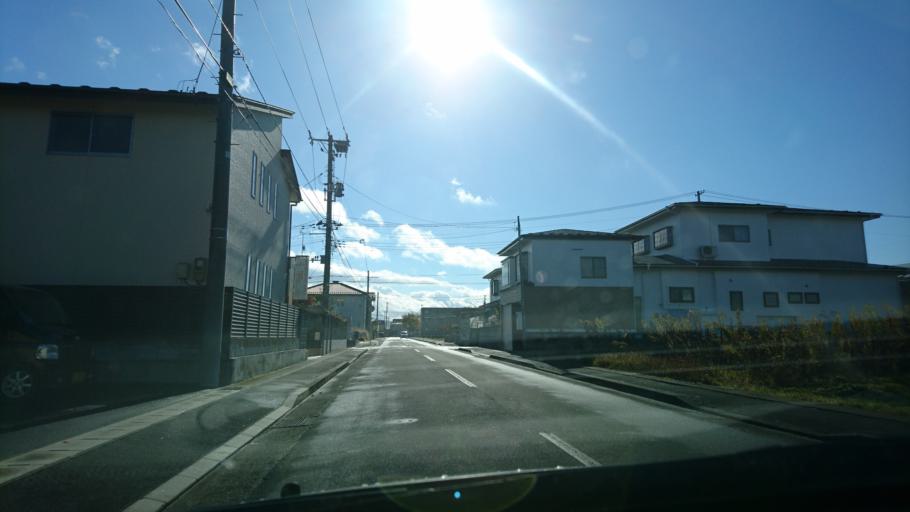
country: JP
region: Iwate
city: Ichinoseki
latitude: 38.9419
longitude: 141.1315
